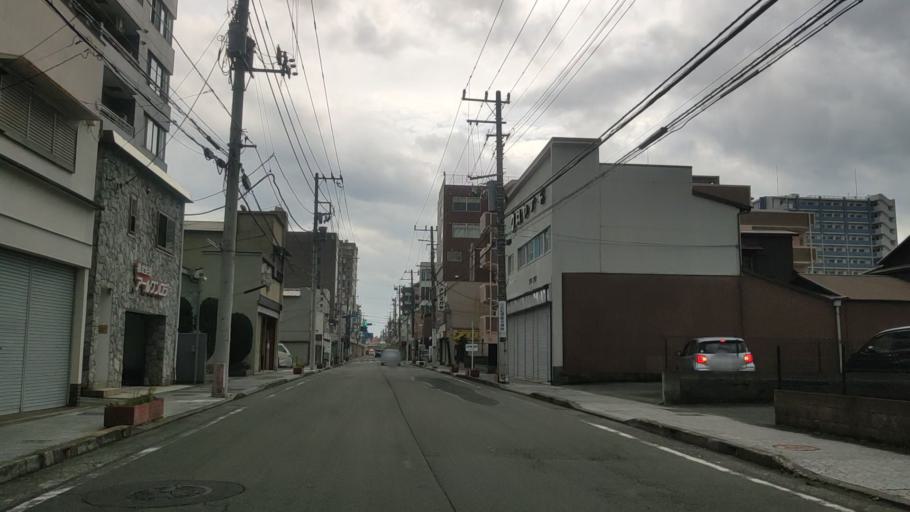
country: JP
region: Kanagawa
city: Odawara
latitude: 35.2534
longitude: 139.1614
